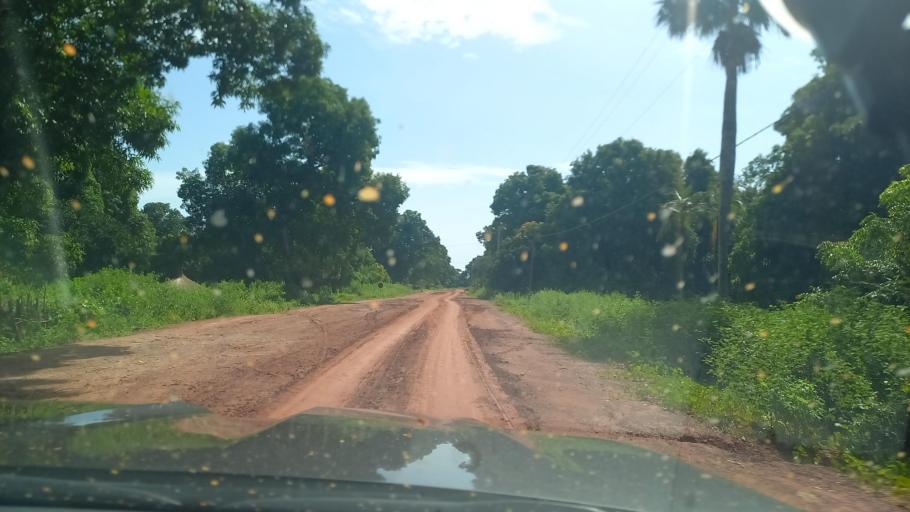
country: SN
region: Ziguinchor
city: Adeane
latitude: 12.6641
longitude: -16.1104
